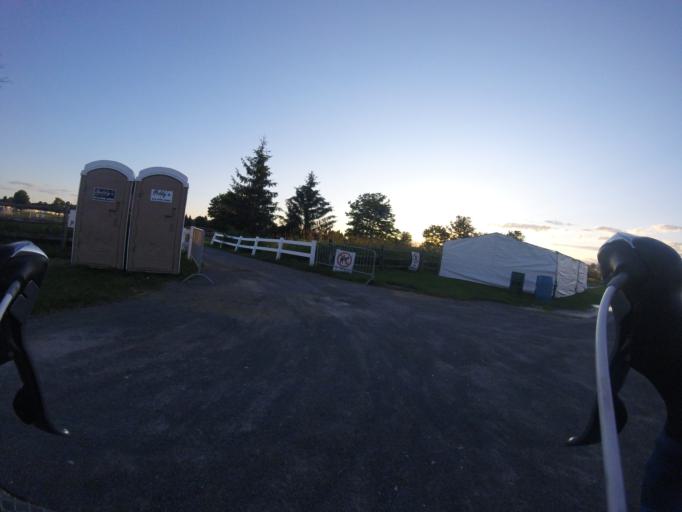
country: CA
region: Ontario
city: Bells Corners
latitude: 45.3390
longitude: -75.8483
